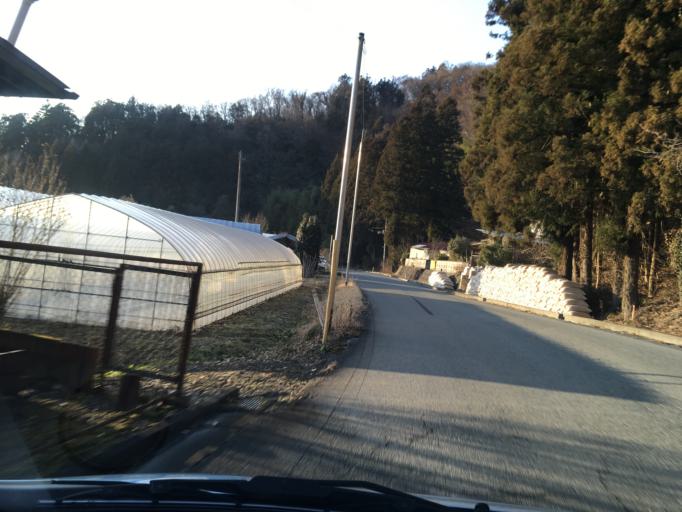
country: JP
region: Iwate
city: Ichinoseki
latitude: 38.8028
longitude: 141.2385
